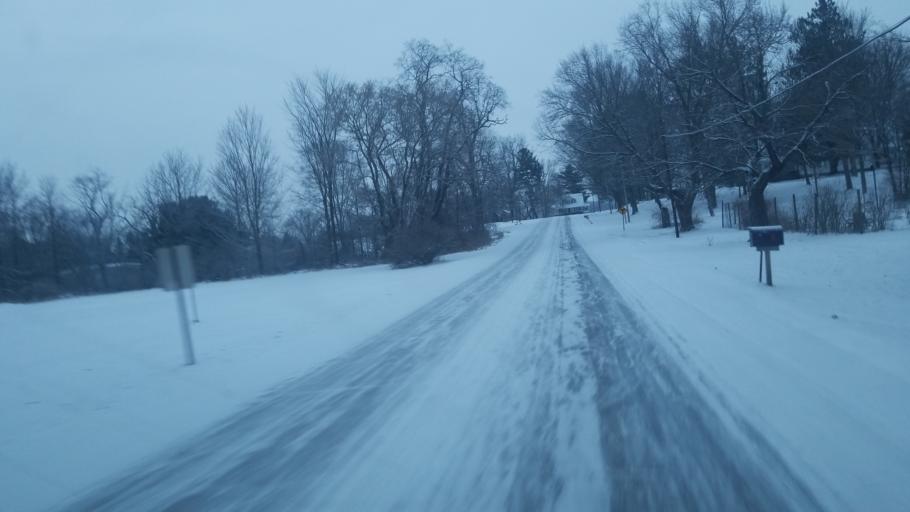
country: US
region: Michigan
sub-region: Osceola County
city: Reed City
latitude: 43.8457
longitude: -85.4445
